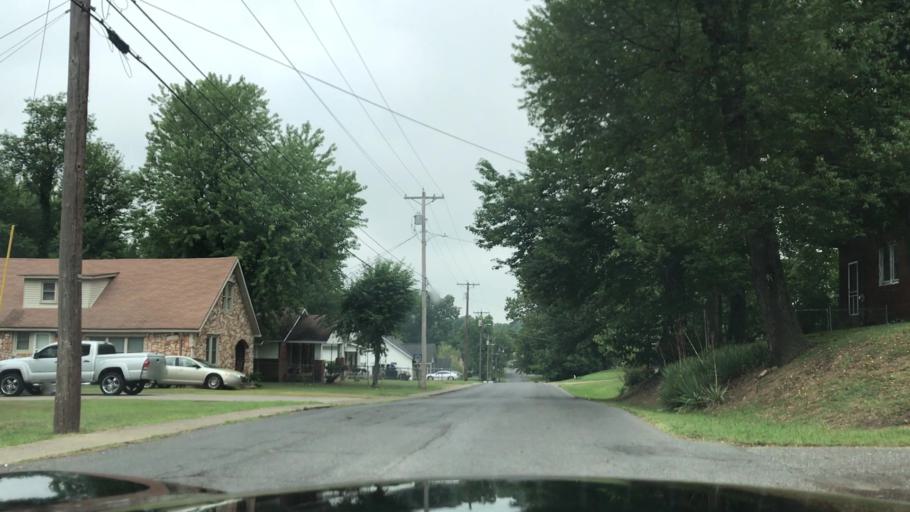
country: US
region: Kentucky
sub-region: Graves County
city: Mayfield
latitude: 36.7316
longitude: -88.6410
